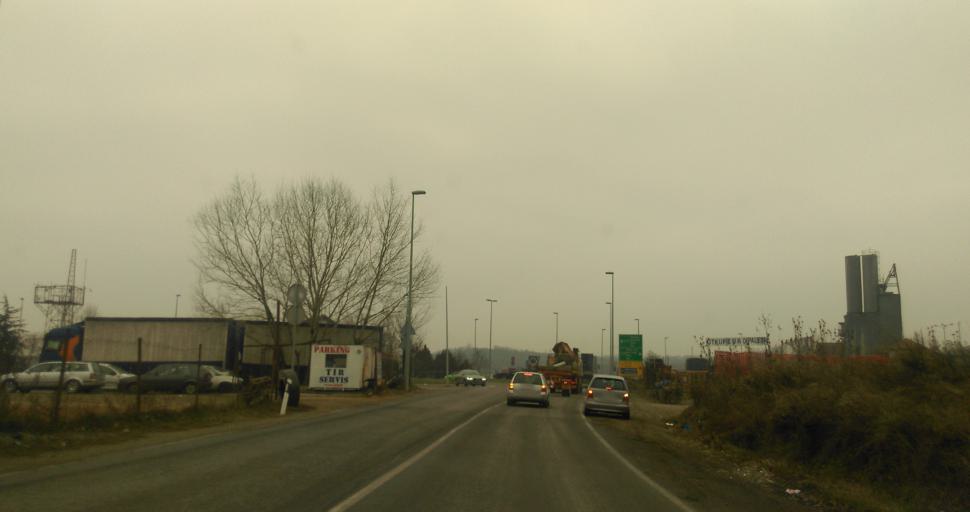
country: RS
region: Central Serbia
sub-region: Belgrade
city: Zvezdara
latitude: 44.7237
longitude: 20.5406
